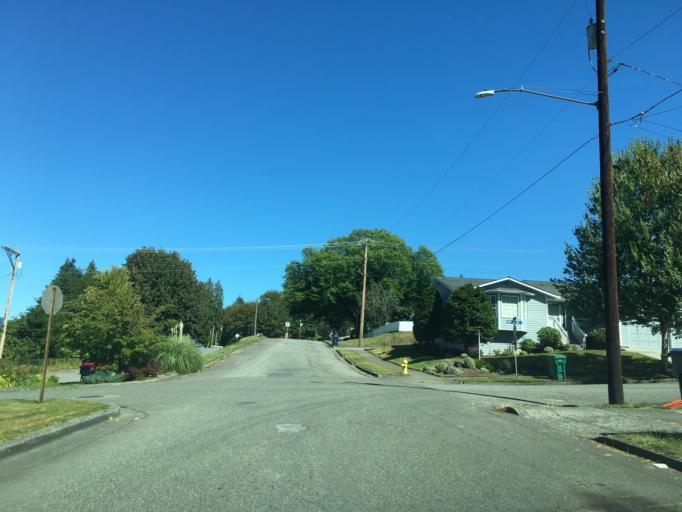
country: US
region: Washington
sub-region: Snohomish County
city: Arlington
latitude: 48.1985
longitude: -122.1241
